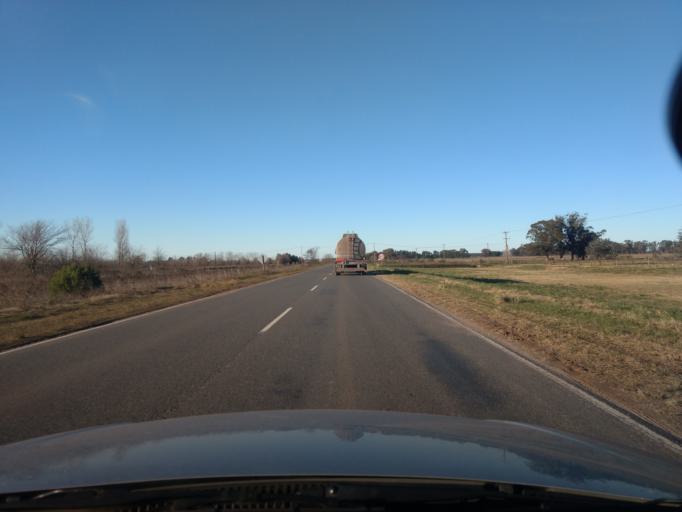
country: AR
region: Buenos Aires
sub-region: Partido de Lujan
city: Lujan
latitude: -34.6405
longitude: -59.1063
